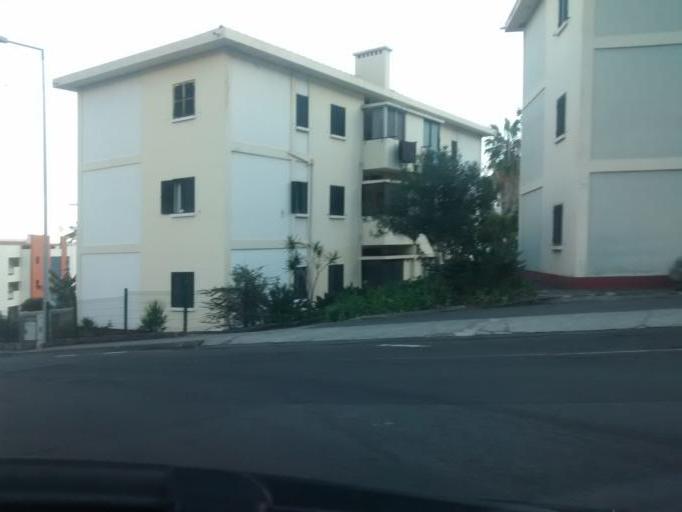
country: PT
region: Madeira
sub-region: Funchal
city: Nossa Senhora do Monte
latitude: 32.6597
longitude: -16.9194
